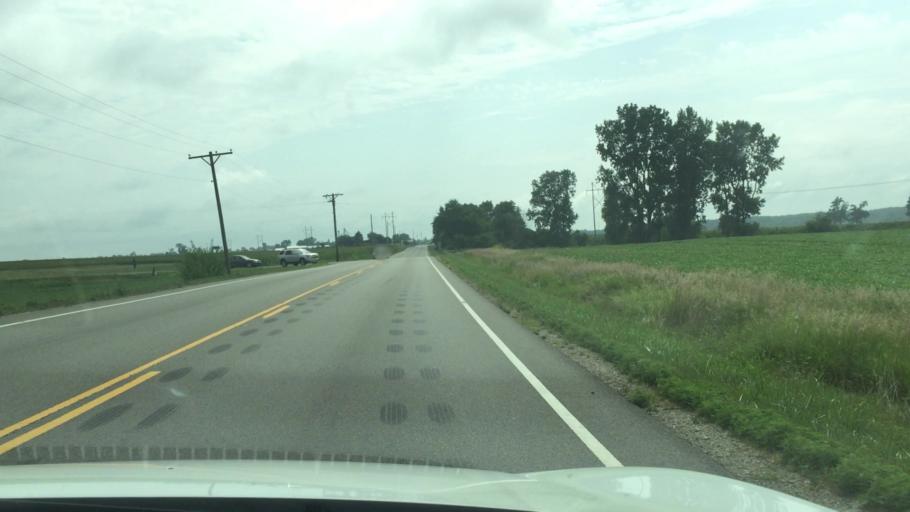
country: US
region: Ohio
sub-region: Champaign County
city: North Lewisburg
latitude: 40.1486
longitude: -83.4635
